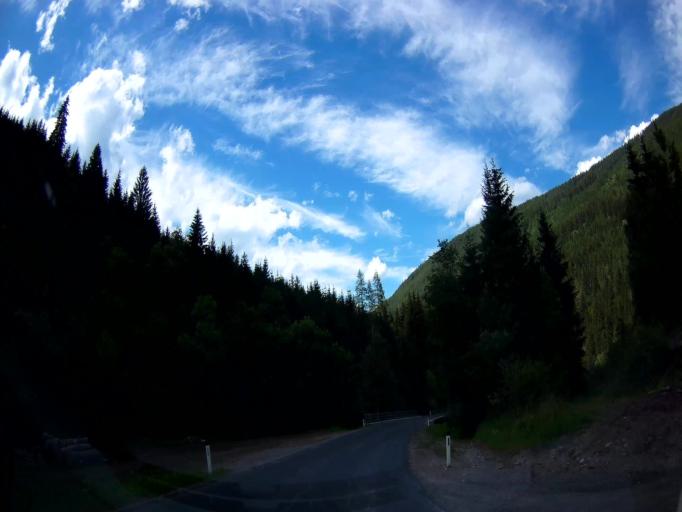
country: AT
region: Styria
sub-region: Politischer Bezirk Murau
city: Stadl an der Mur
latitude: 47.0459
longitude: 13.9998
